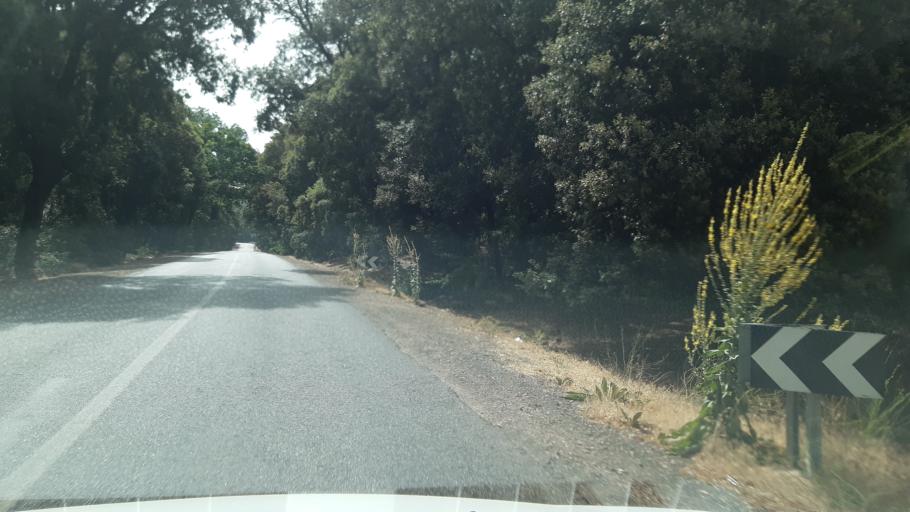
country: MA
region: Meknes-Tafilalet
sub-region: Ifrane
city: Azrou
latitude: 33.4344
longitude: -5.1813
